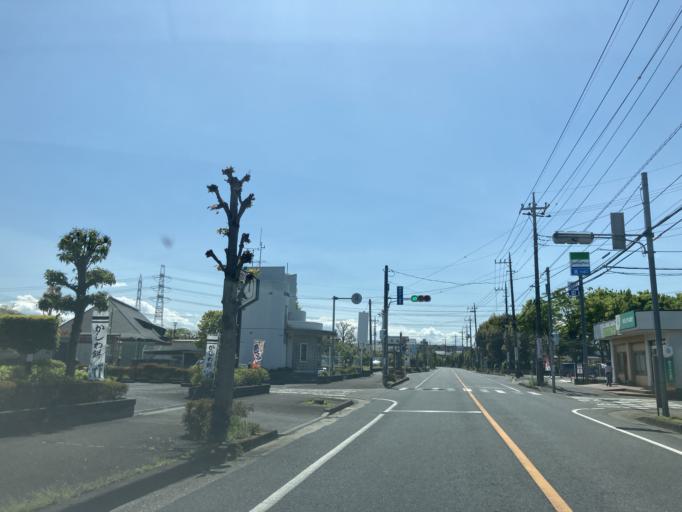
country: JP
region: Saitama
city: Sayama
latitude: 35.8822
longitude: 139.4114
